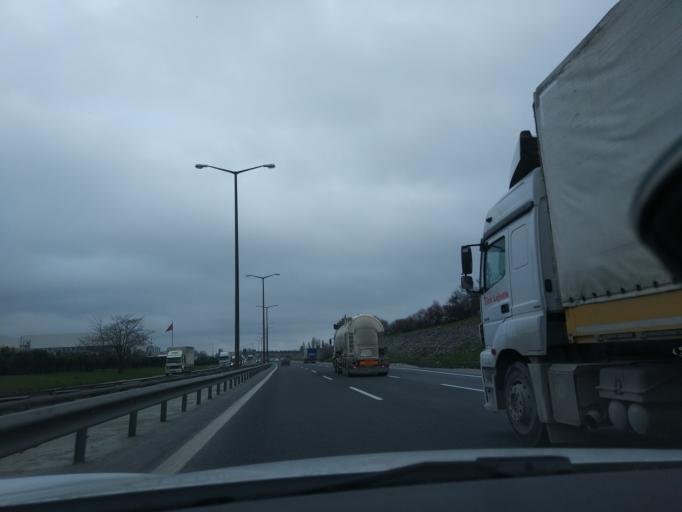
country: TR
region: Istanbul
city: Esenyurt
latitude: 41.0710
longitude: 28.6490
